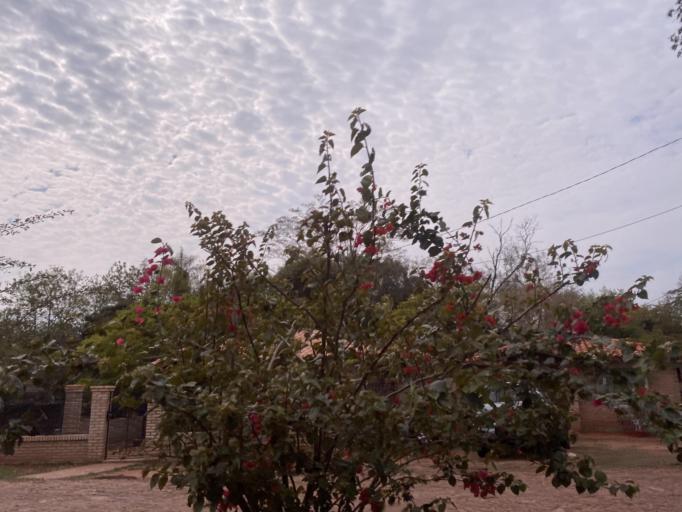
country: PY
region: Misiones
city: San Juan Bautista
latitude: -26.6771
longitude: -57.1372
